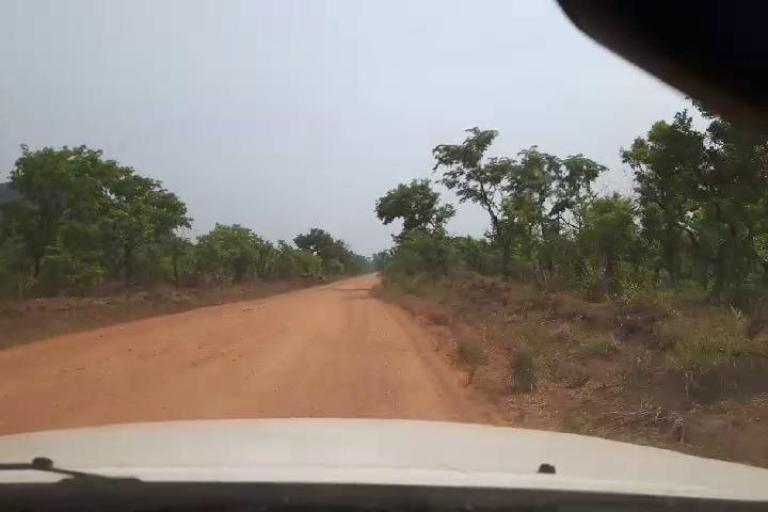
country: SL
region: Northern Province
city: Masingbi
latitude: 8.8886
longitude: -11.8186
